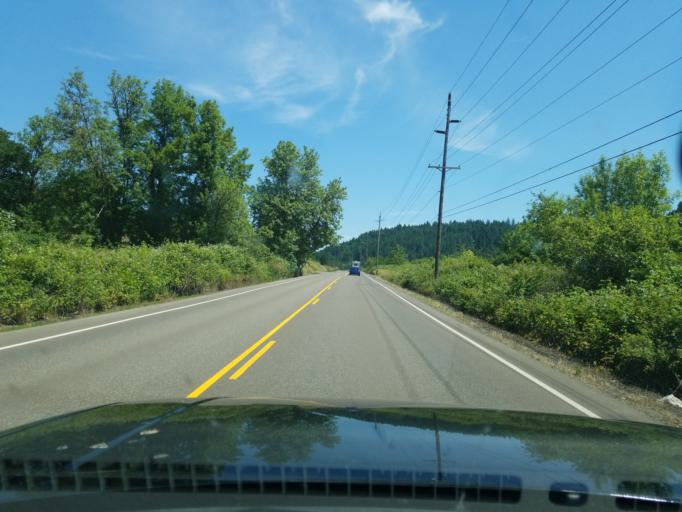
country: US
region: Oregon
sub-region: Yamhill County
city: Yamhill
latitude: 45.3785
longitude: -123.1483
